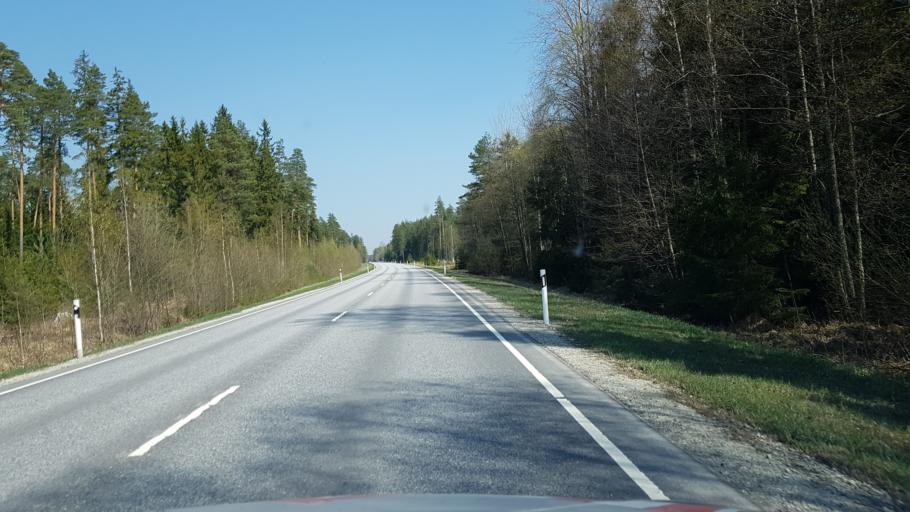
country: EE
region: Paernumaa
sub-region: Vaendra vald (alev)
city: Vandra
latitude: 58.6844
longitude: 25.2383
